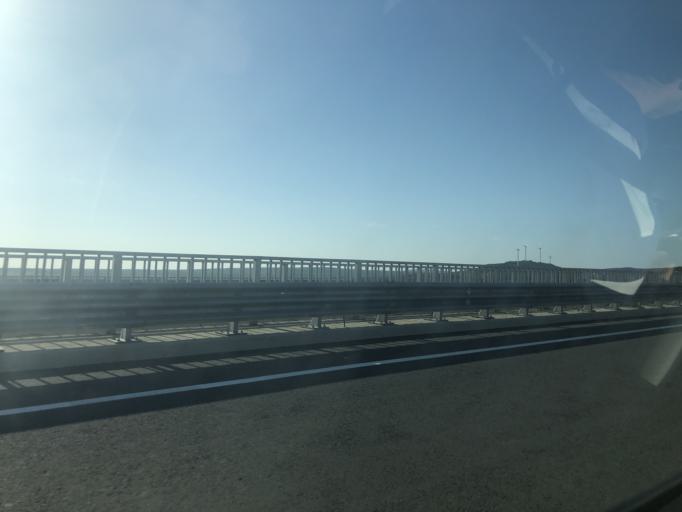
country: TR
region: Istanbul
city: Catalca
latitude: 41.1894
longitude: 28.4633
